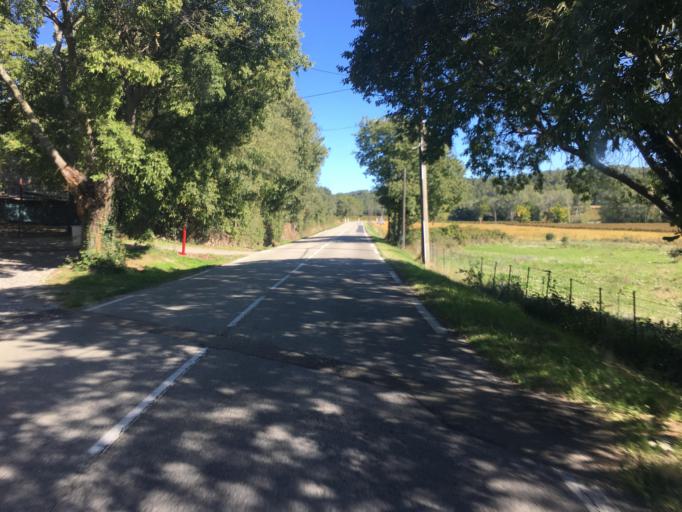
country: FR
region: Languedoc-Roussillon
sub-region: Departement du Gard
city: Quissac
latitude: 43.9232
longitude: 4.0384
